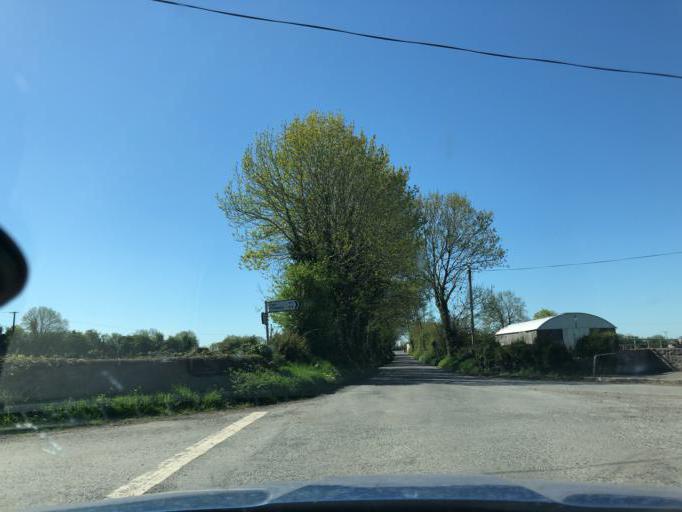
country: IE
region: Connaught
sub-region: County Galway
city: Portumna
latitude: 53.1507
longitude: -8.3382
